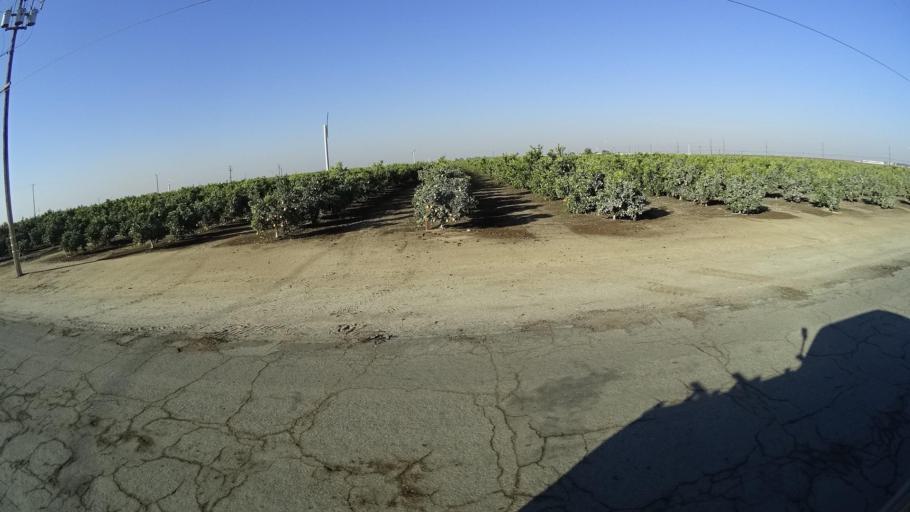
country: US
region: California
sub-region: Tulare County
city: Richgrove
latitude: 35.7733
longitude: -119.1518
